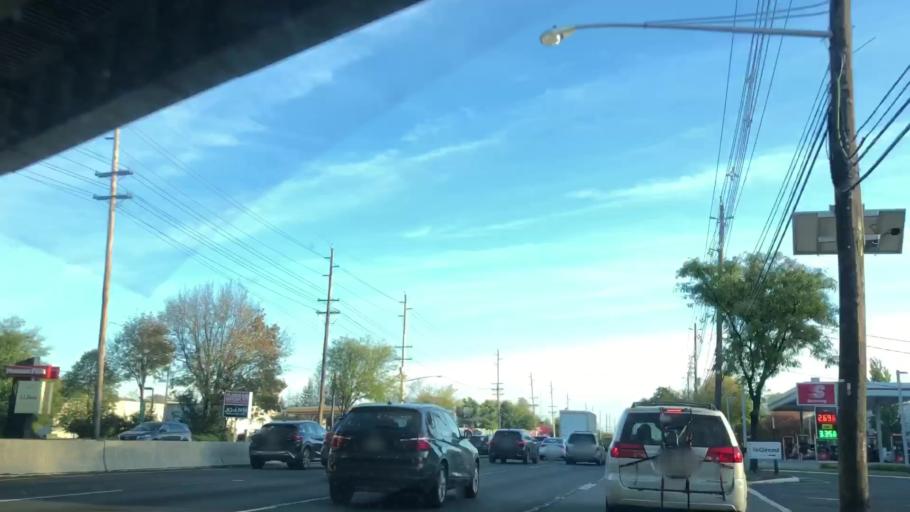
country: US
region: New Jersey
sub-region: Bergen County
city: Paramus
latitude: 40.9599
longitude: -74.0756
